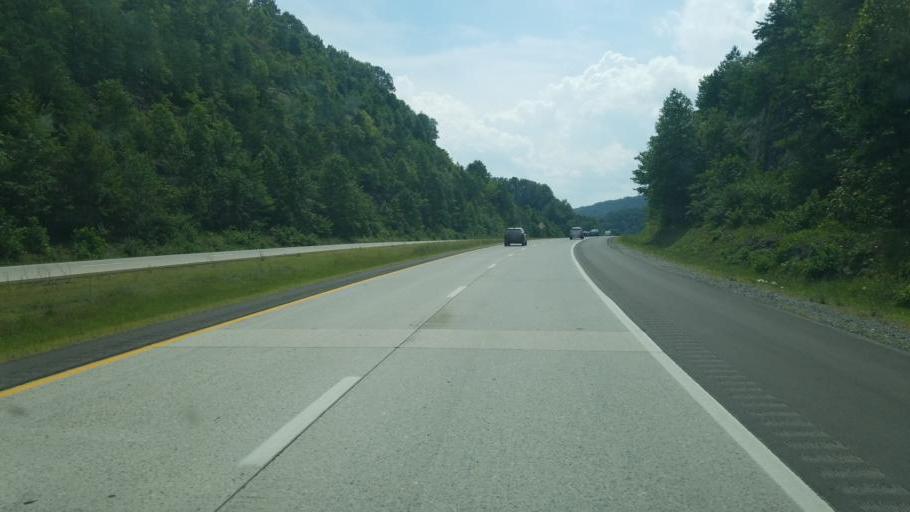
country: US
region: West Virginia
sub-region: Kanawha County
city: Alum Creek
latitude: 38.2024
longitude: -81.8342
